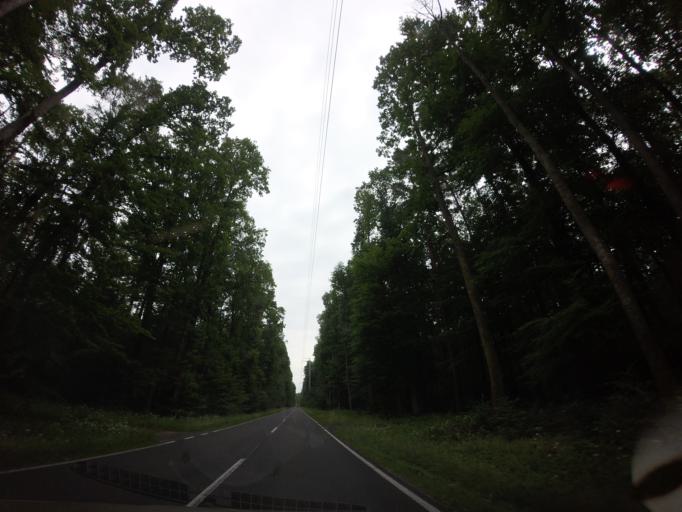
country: PL
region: West Pomeranian Voivodeship
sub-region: Powiat drawski
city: Wierzchowo
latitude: 53.4069
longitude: 16.1918
